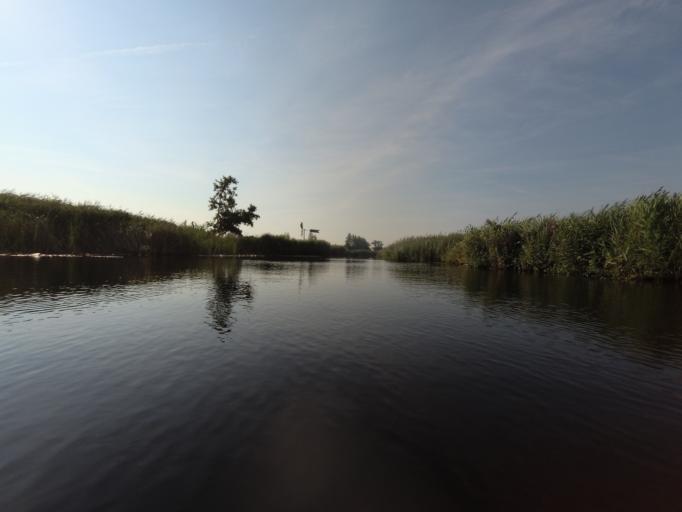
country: NL
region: Overijssel
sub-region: Gemeente Steenwijkerland
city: Sint Jansklooster
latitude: 52.6653
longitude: 6.0644
